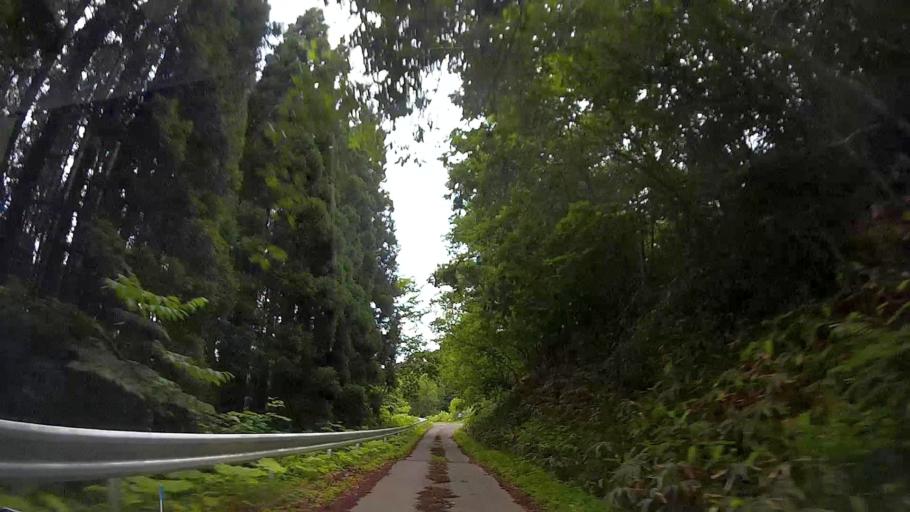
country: JP
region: Hokkaido
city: Nanae
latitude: 42.1246
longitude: 140.4199
